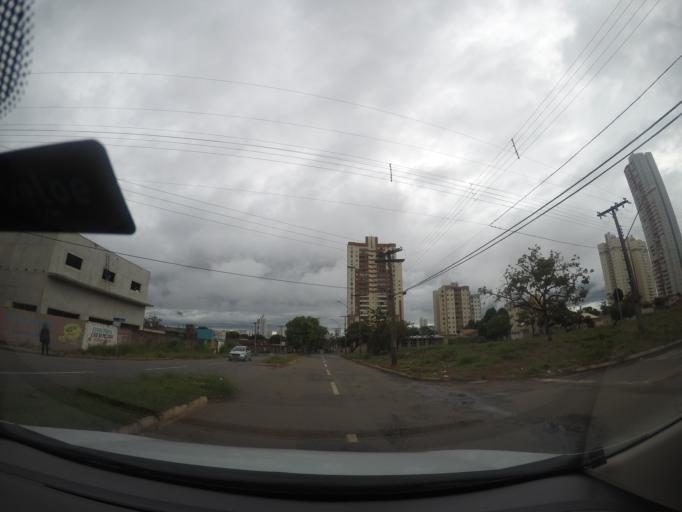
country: BR
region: Goias
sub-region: Goiania
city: Goiania
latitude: -16.7323
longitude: -49.2859
